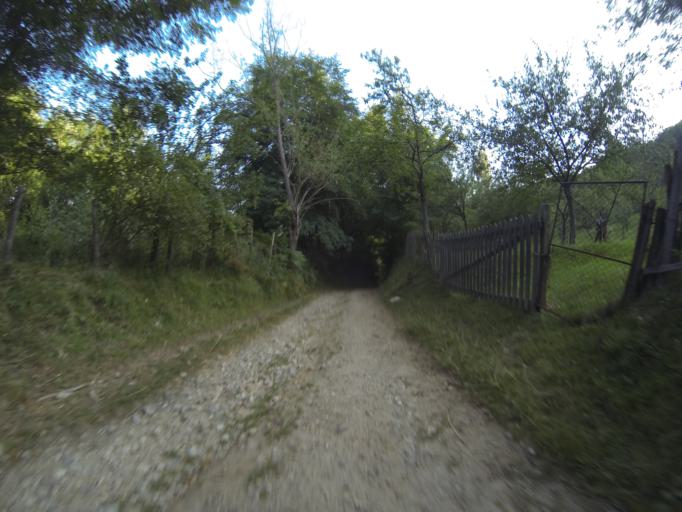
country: RO
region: Valcea
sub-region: Comuna Horezu
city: Horezu
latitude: 45.1911
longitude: 23.9862
